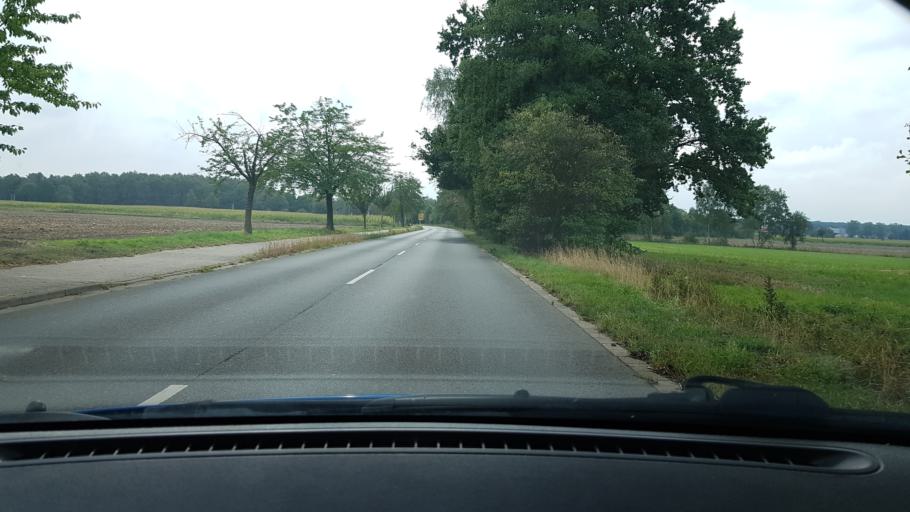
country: DE
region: Lower Saxony
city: Garbsen
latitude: 52.4353
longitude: 9.5742
